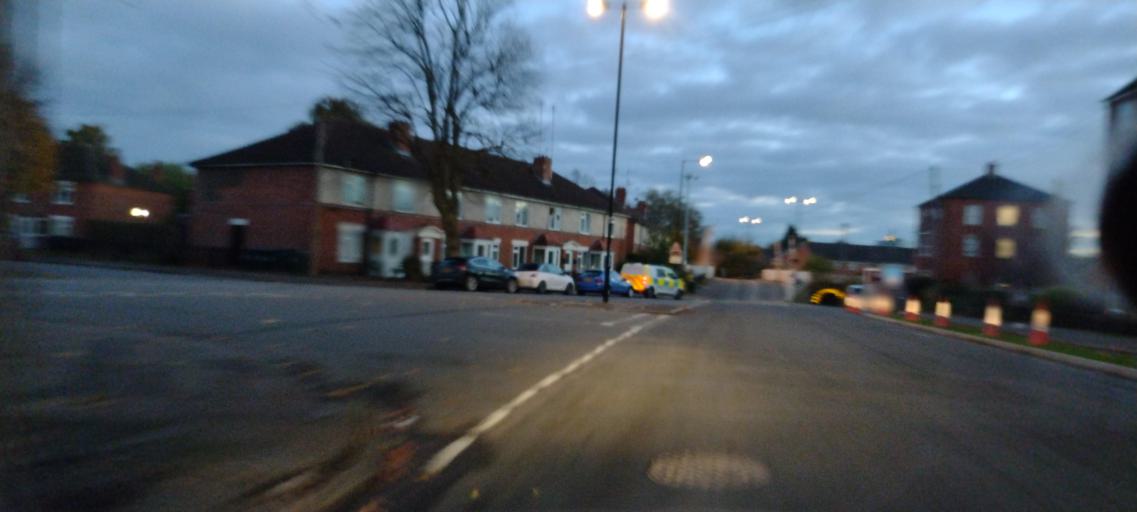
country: GB
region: England
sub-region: Coventry
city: Coventry
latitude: 52.4145
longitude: -1.5236
